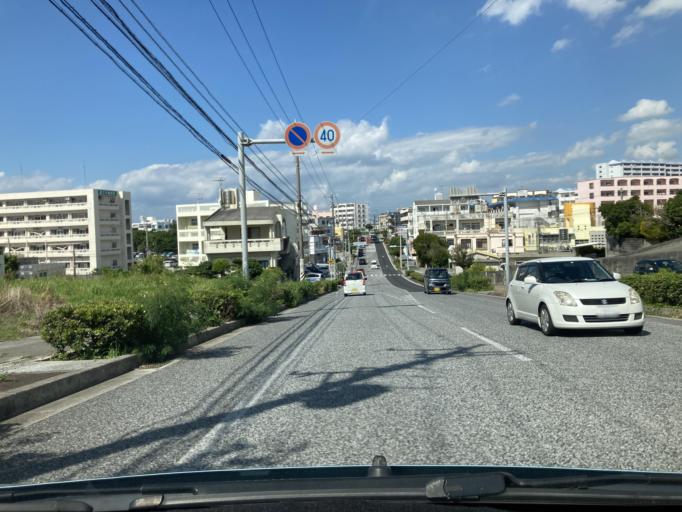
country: JP
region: Okinawa
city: Ginowan
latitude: 26.2516
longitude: 127.7575
